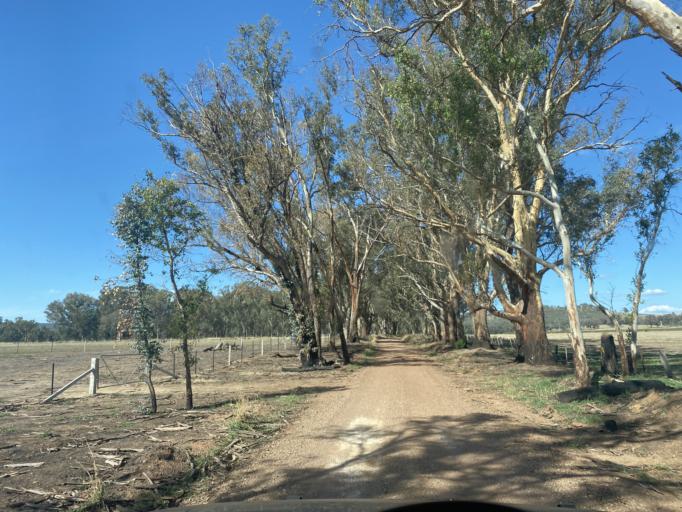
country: AU
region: Victoria
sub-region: Benalla
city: Benalla
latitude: -36.7373
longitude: 146.0578
